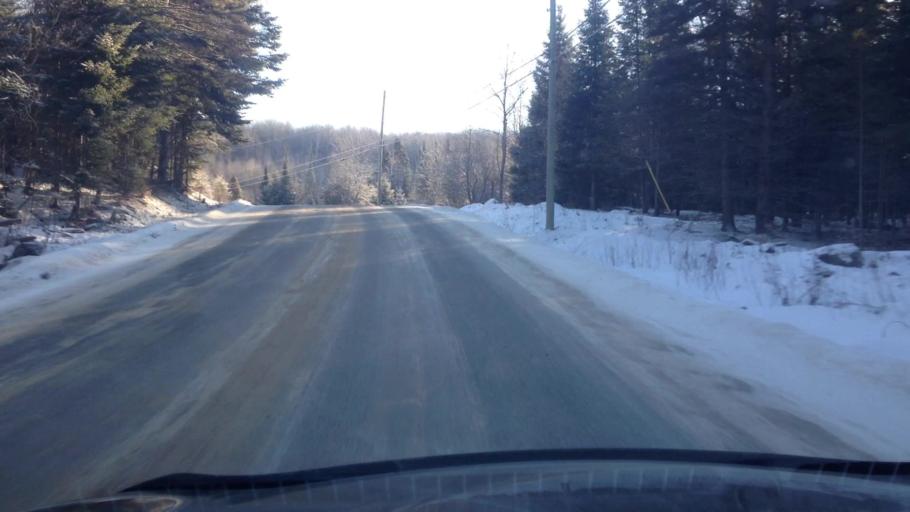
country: CA
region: Quebec
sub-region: Laurentides
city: Brownsburg-Chatham
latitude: 45.9205
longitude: -74.5248
